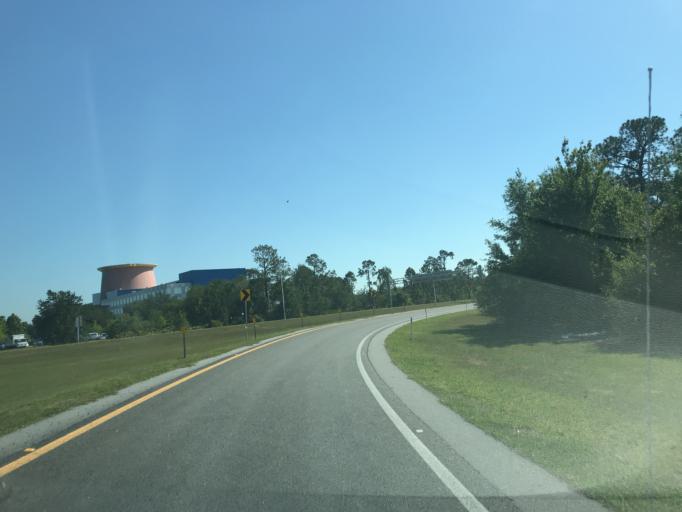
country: US
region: Florida
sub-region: Osceola County
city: Celebration
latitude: 28.3623
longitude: -81.5226
